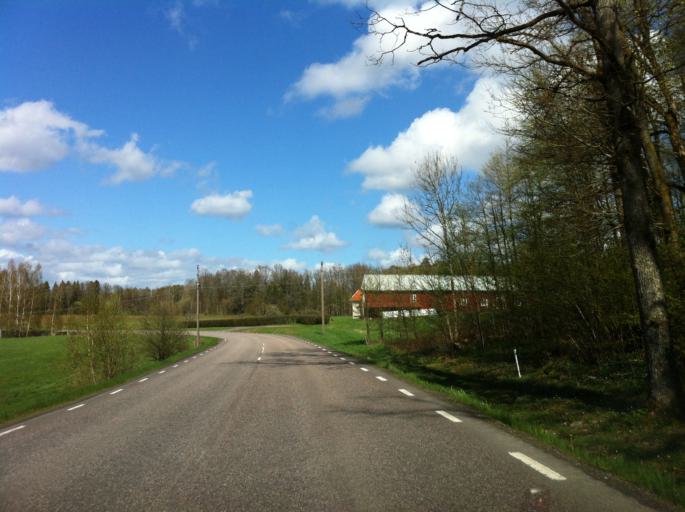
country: SE
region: Vaestra Goetaland
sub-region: Alingsas Kommun
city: Alingsas
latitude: 57.8646
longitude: 12.5692
